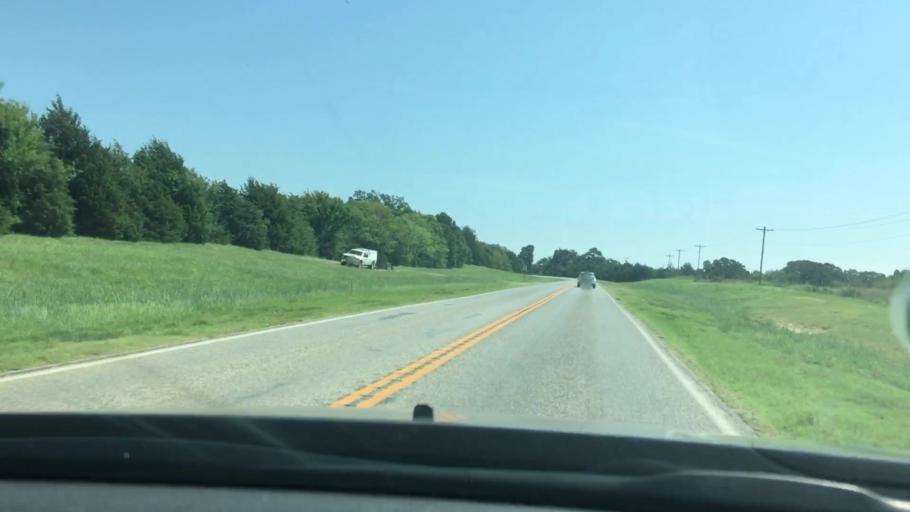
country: US
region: Oklahoma
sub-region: Johnston County
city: Tishomingo
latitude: 34.2301
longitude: -96.6313
